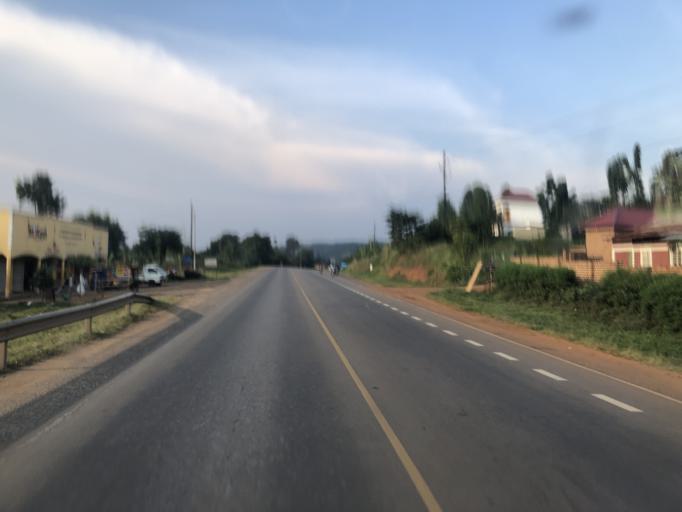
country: UG
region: Central Region
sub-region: Mpigi District
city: Mpigi
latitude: 0.1998
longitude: 32.2998
